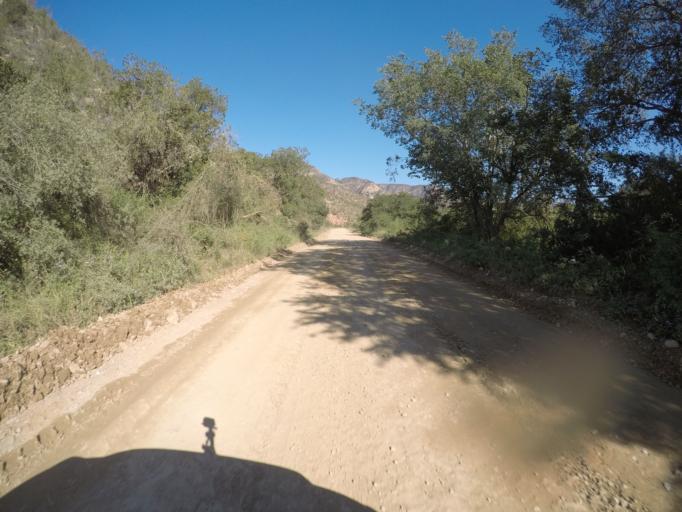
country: ZA
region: Eastern Cape
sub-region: Cacadu District Municipality
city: Kareedouw
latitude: -33.6644
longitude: 24.5458
